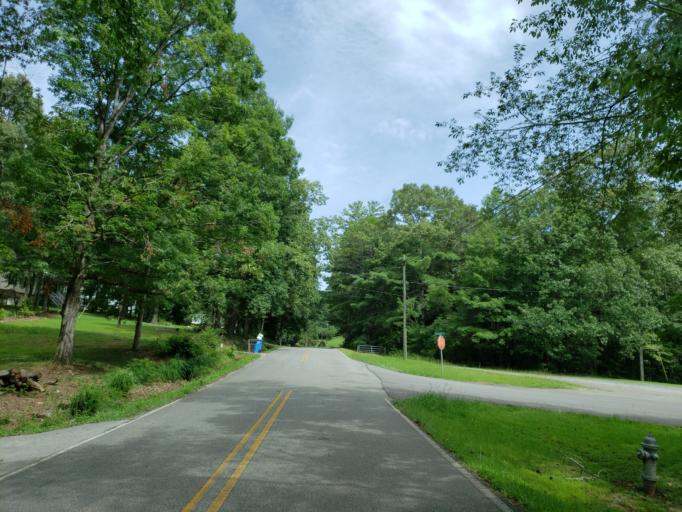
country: US
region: Georgia
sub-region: Pickens County
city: Nelson
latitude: 34.3698
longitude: -84.3815
